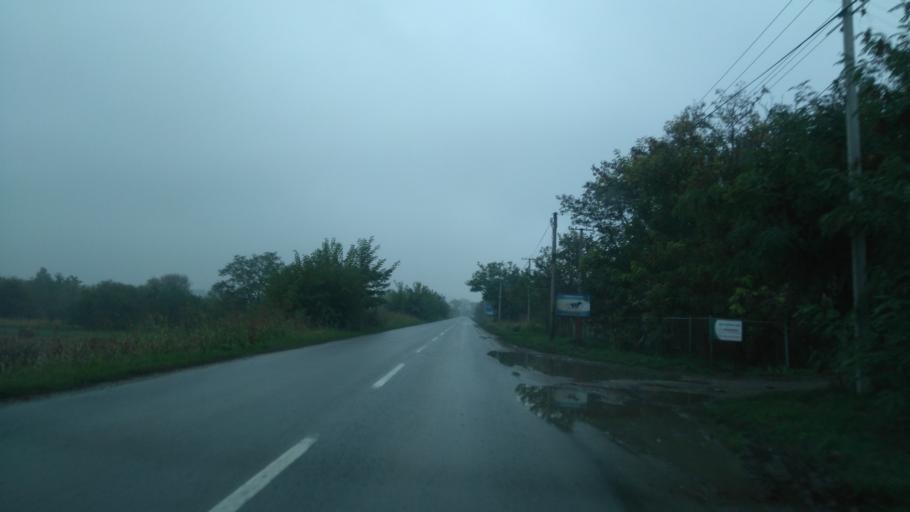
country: RS
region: Autonomna Pokrajina Vojvodina
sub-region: Juznobacki Okrug
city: Becej
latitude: 45.6497
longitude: 20.0363
